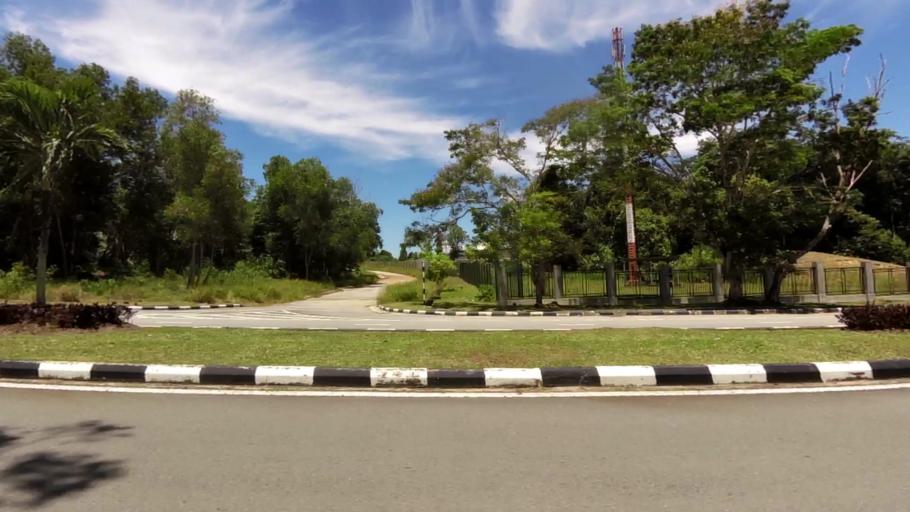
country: BN
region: Brunei and Muara
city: Bandar Seri Begawan
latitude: 4.9222
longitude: 114.9399
